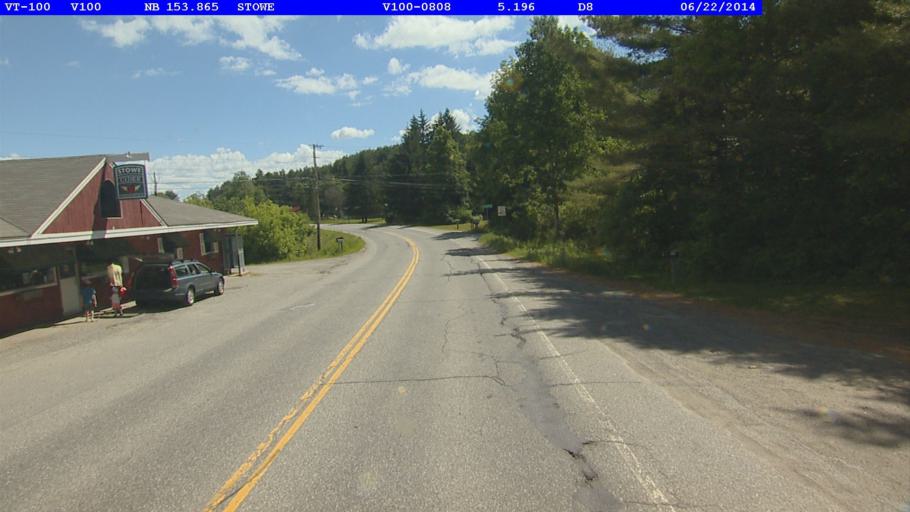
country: US
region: Vermont
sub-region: Lamoille County
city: Morristown
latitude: 44.4828
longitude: -72.6617
